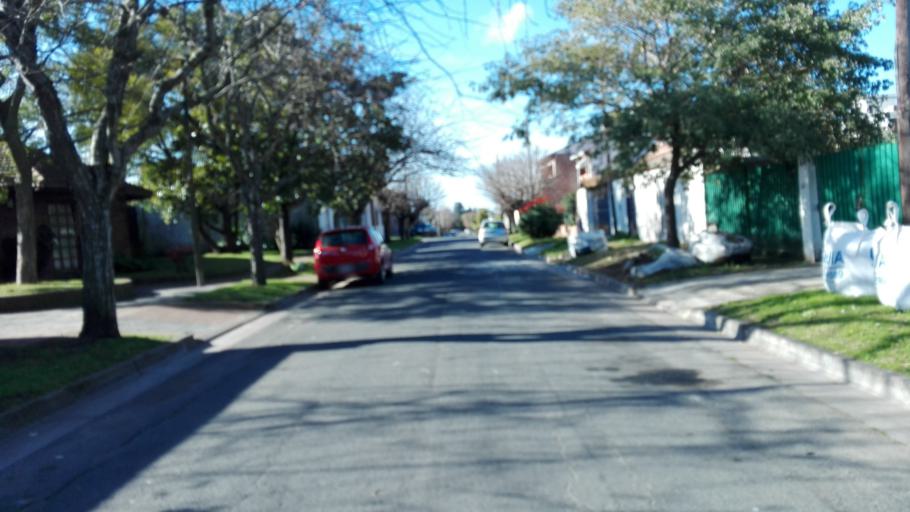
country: AR
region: Buenos Aires
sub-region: Partido de La Plata
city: La Plata
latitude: -34.8873
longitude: -57.9946
